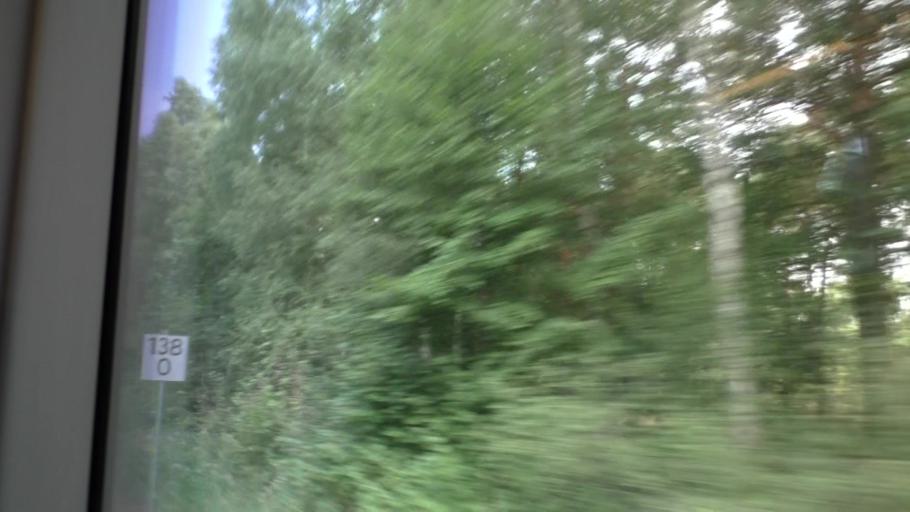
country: DE
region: Brandenburg
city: Mullrose
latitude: 52.2331
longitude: 14.4306
